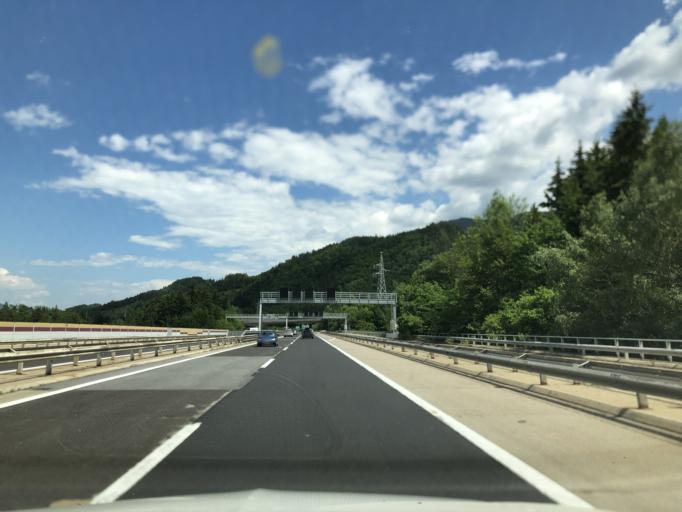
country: AT
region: Carinthia
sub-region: Politischer Bezirk Villach Land
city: Hohenthurn
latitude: 46.5382
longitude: 13.6569
